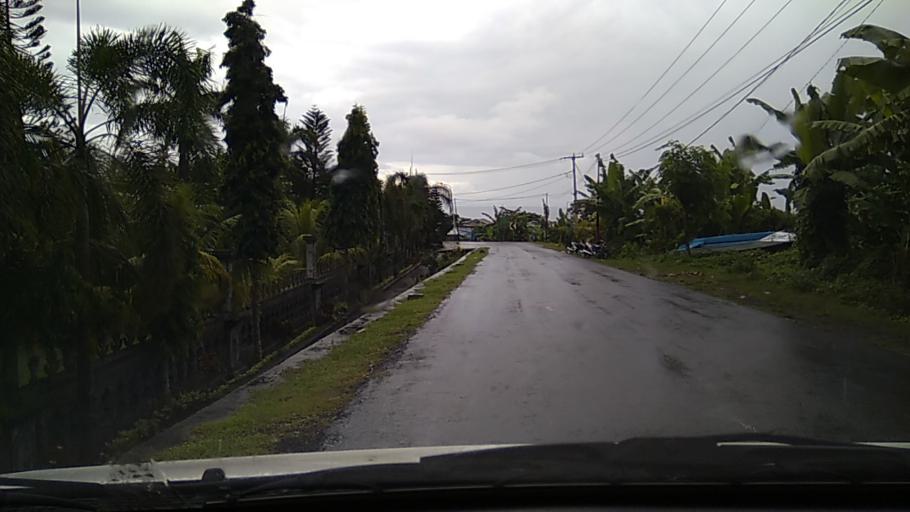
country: ID
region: Bali
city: Banjar Danginsema
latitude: -8.4659
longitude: 115.6311
